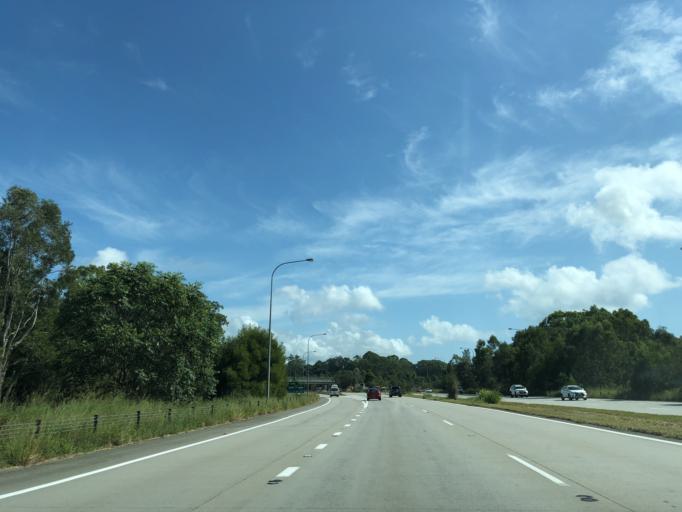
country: AU
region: New South Wales
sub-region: Byron Shire
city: Brunswick Heads
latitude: -28.5624
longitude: 153.5423
